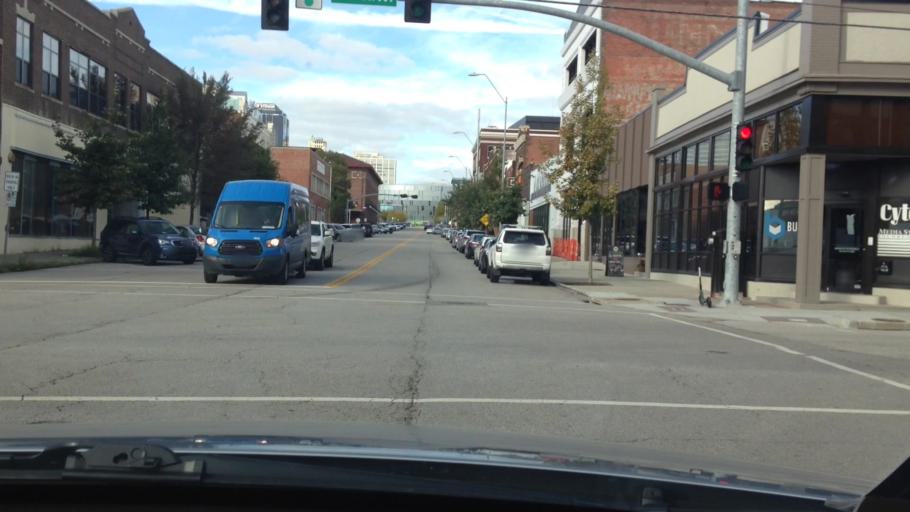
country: US
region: Missouri
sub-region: Jackson County
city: Kansas City
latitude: 39.0903
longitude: -94.5802
